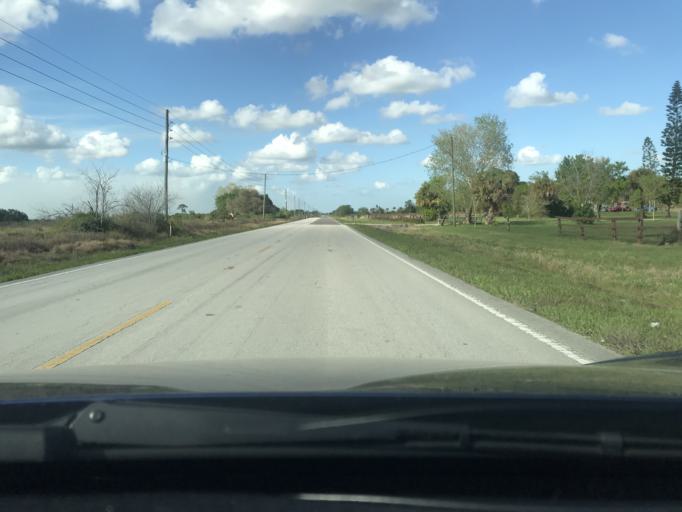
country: US
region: Florida
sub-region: Okeechobee County
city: Taylor Creek
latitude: 27.2502
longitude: -80.6945
